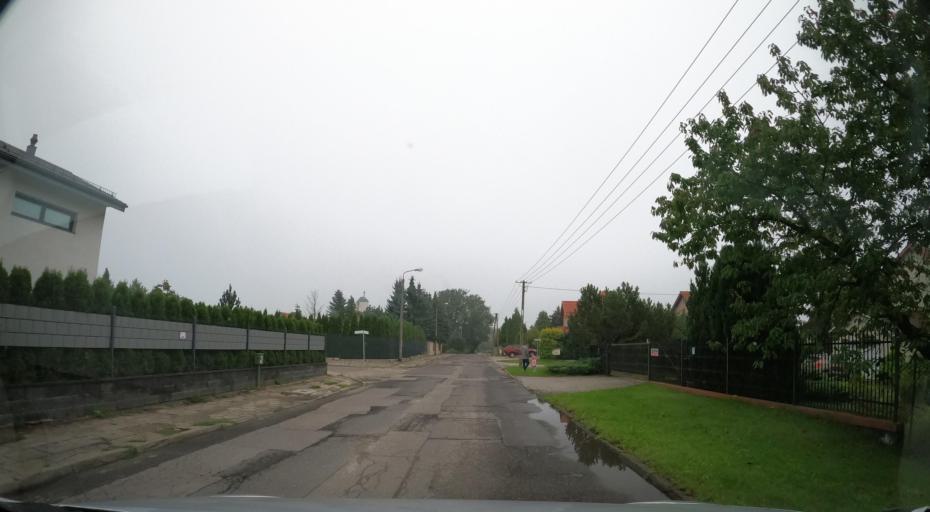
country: PL
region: Pomeranian Voivodeship
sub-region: Powiat kartuski
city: Chwaszczyno
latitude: 54.4257
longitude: 18.4609
